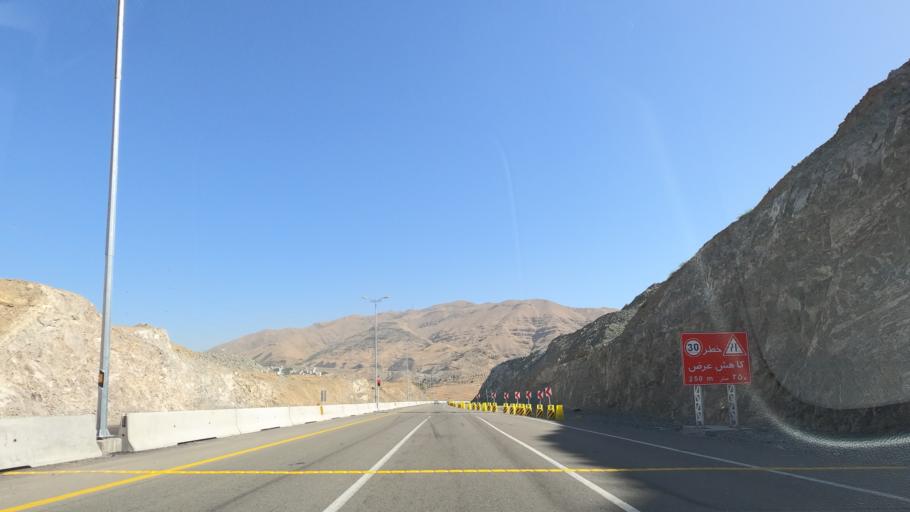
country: IR
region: Alborz
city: Karaj
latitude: 35.8192
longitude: 51.0378
